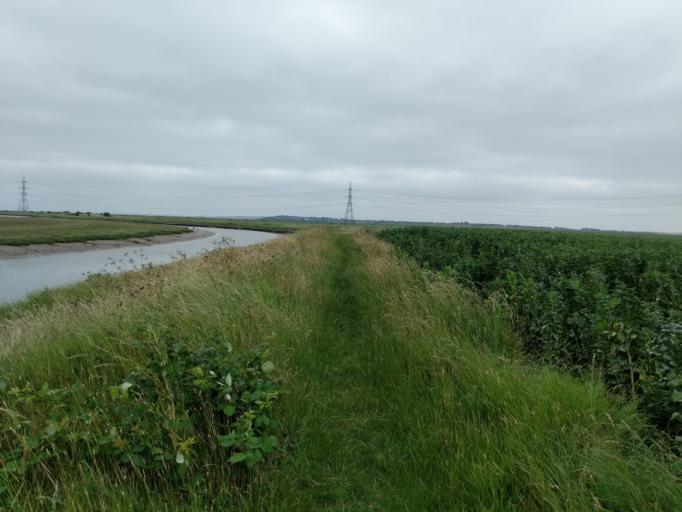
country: GB
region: England
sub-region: Kent
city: Faversham
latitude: 51.3330
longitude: 0.9128
